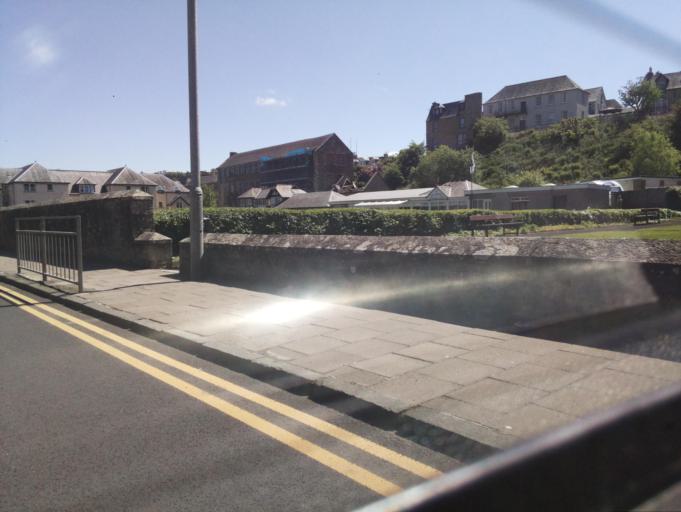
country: GB
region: Scotland
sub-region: The Scottish Borders
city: Hawick
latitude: 55.4211
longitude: -2.7952
